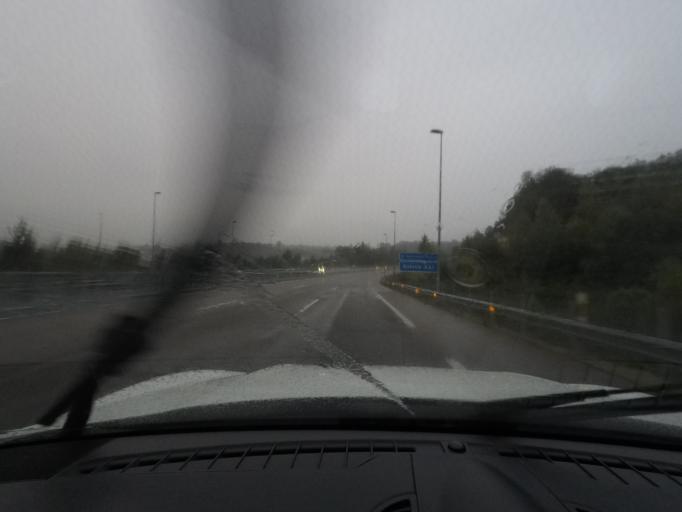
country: ES
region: Asturias
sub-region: Province of Asturias
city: Oviedo
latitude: 43.3444
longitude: -5.8674
